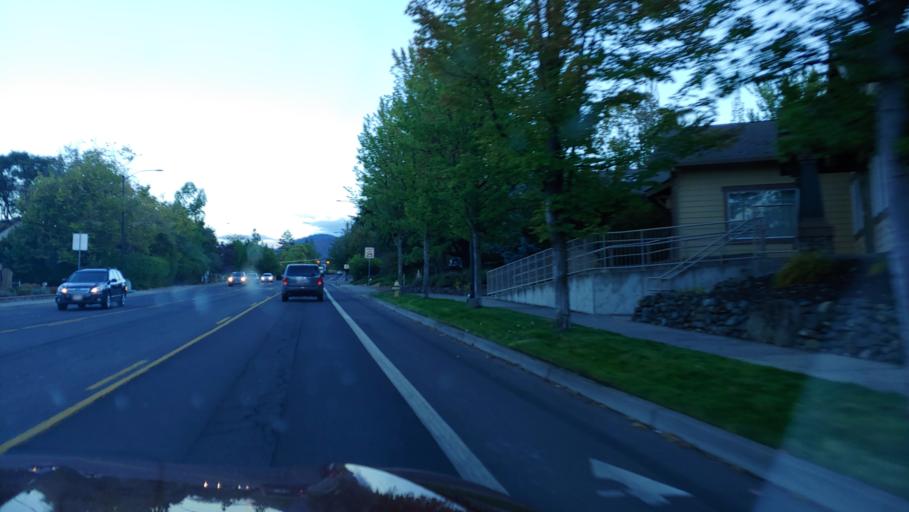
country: US
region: Oregon
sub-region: Jackson County
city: Ashland
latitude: 42.2086
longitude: -122.7232
